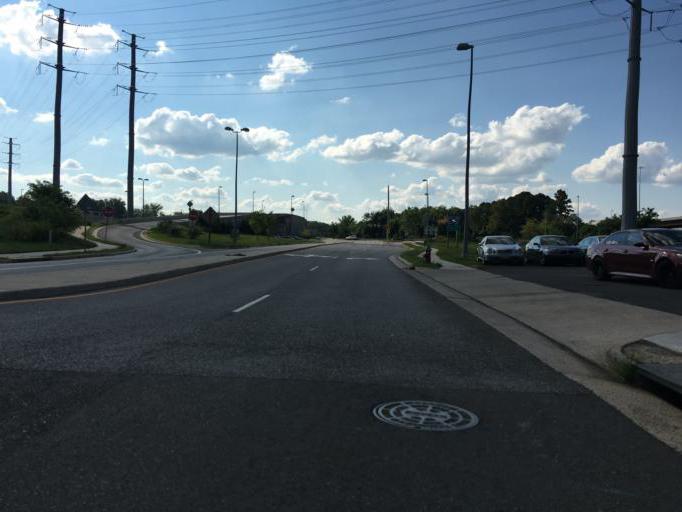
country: US
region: Virginia
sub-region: Fairfax County
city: Huntington
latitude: 38.7978
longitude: -77.0782
